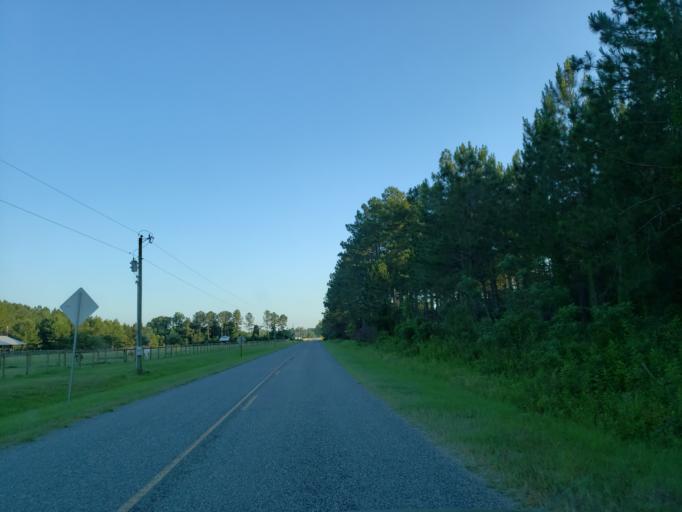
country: US
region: Georgia
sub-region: Dooly County
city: Vienna
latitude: 32.1062
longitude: -83.7555
